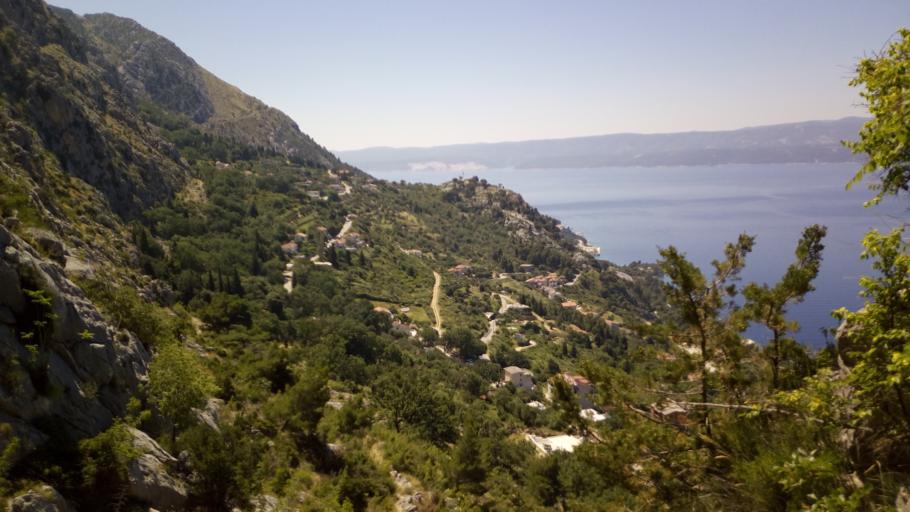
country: HR
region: Splitsko-Dalmatinska
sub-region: Grad Omis
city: Omis
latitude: 43.4438
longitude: 16.7032
